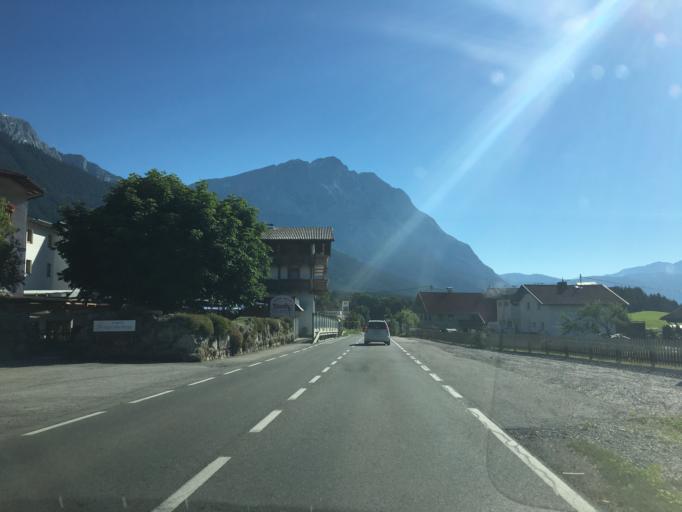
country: AT
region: Tyrol
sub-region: Politischer Bezirk Innsbruck Land
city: Wildermieming
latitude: 47.3115
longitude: 11.0023
